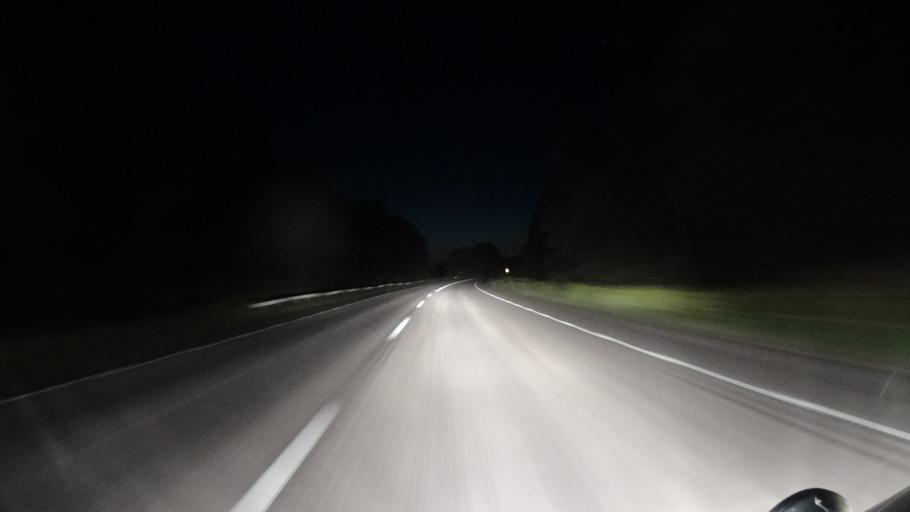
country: SE
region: OEstergoetland
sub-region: Vadstena Kommun
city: Herrestad
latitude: 58.2793
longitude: 14.7583
